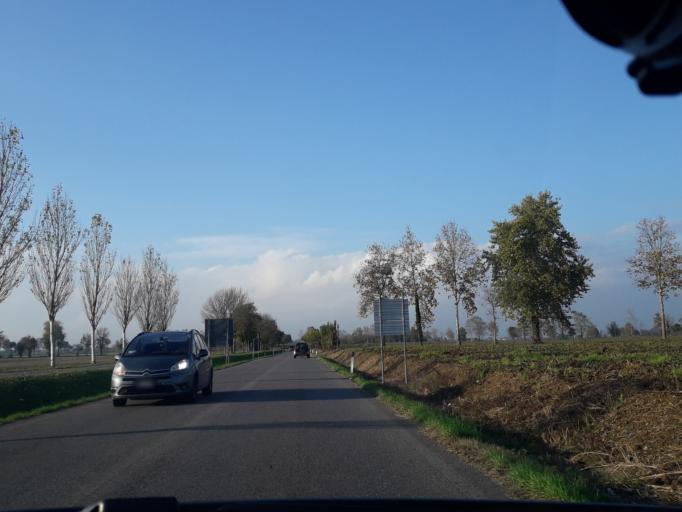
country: IT
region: Friuli Venezia Giulia
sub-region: Provincia di Udine
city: Pradamano
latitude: 46.0388
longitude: 13.2911
